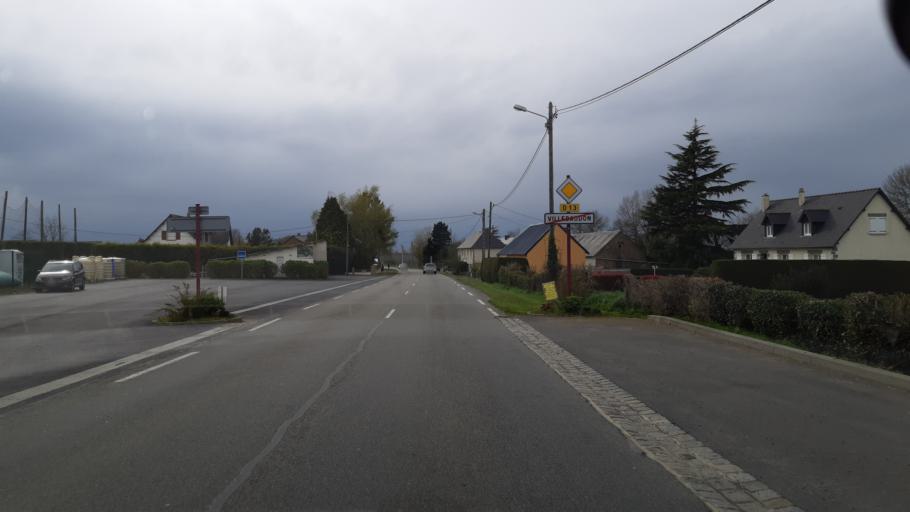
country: FR
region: Lower Normandy
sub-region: Departement de la Manche
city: Percy
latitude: 48.9603
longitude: -1.1686
